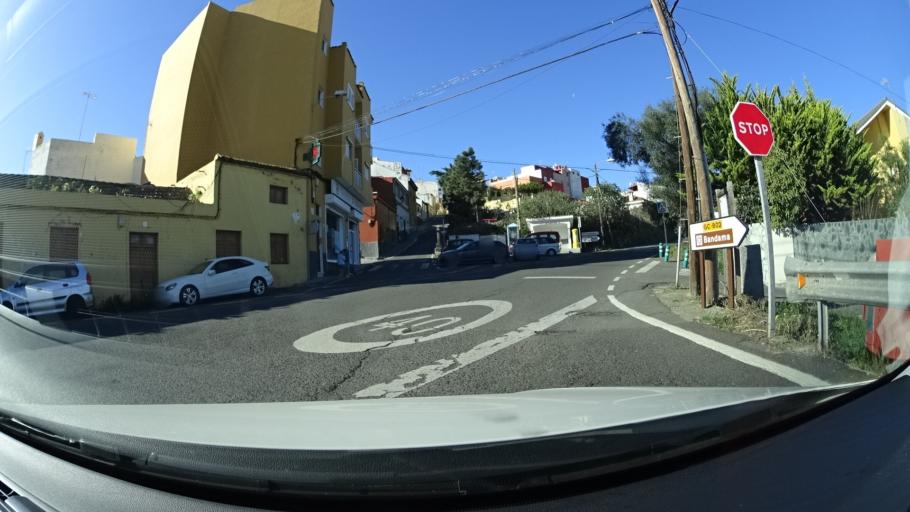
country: ES
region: Canary Islands
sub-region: Provincia de Las Palmas
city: Santa Brigida
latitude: 28.0277
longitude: -15.4763
